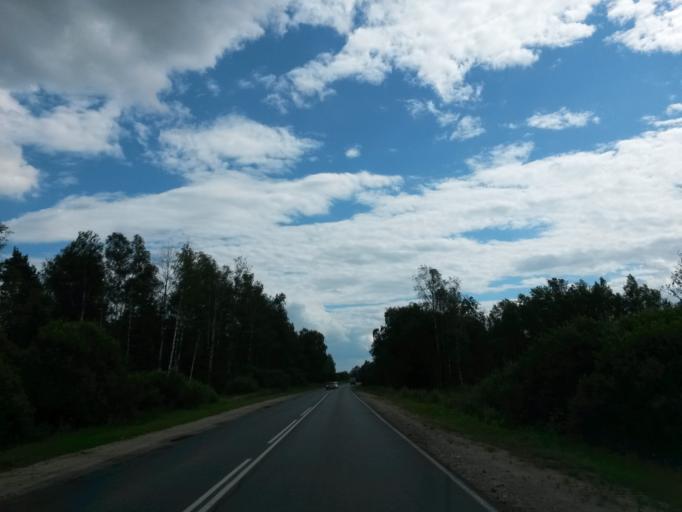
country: RU
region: Ivanovo
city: Novo-Talitsy
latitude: 57.0724
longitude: 40.6878
